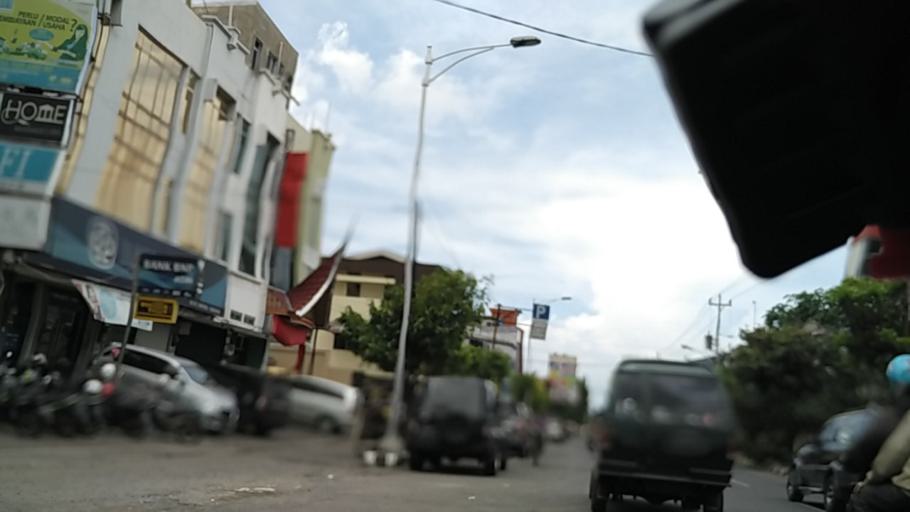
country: ID
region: Central Java
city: Semarang
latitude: -6.9840
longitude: 110.4316
